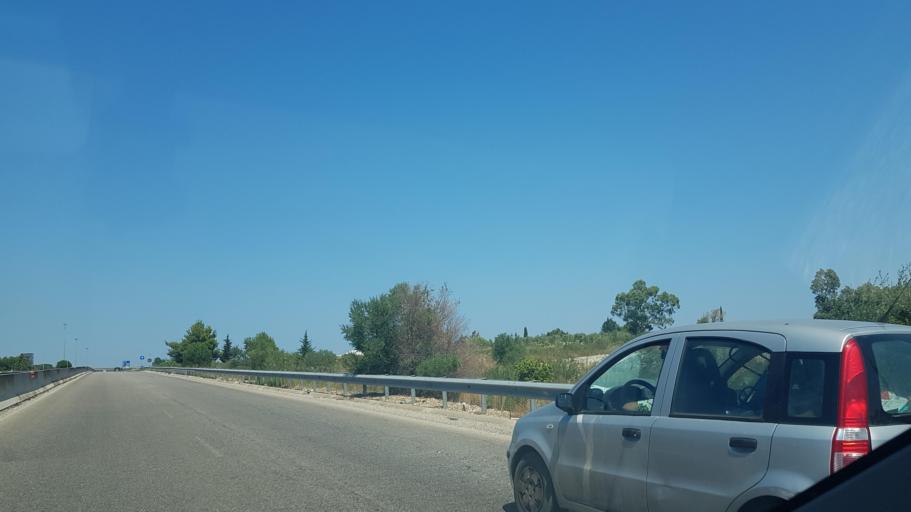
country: IT
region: Apulia
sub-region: Provincia di Lecce
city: Merine
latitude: 40.3456
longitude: 18.2047
